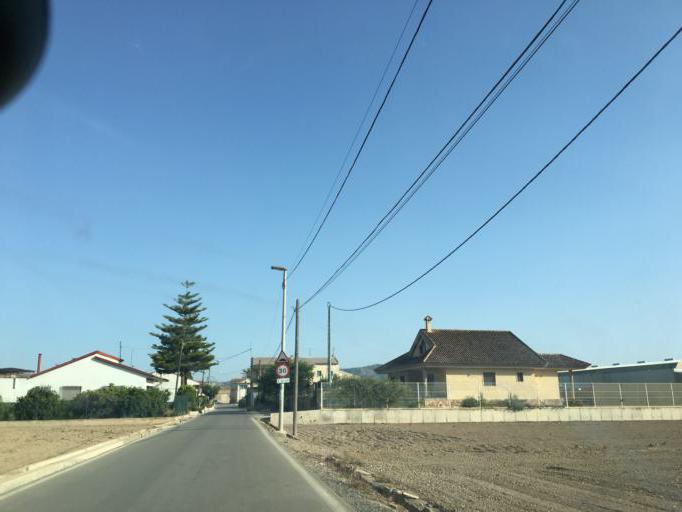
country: ES
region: Murcia
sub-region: Murcia
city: Santomera
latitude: 38.0301
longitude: -1.0673
